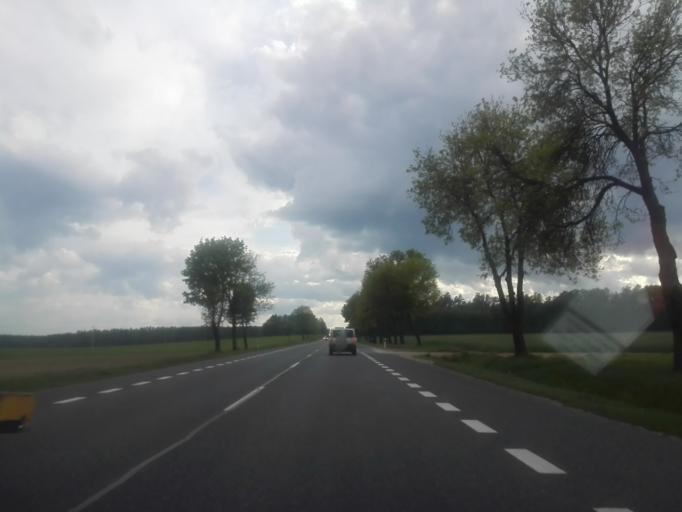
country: PL
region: Podlasie
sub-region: Powiat zambrowski
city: Szumowo
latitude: 52.8649
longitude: 22.0097
